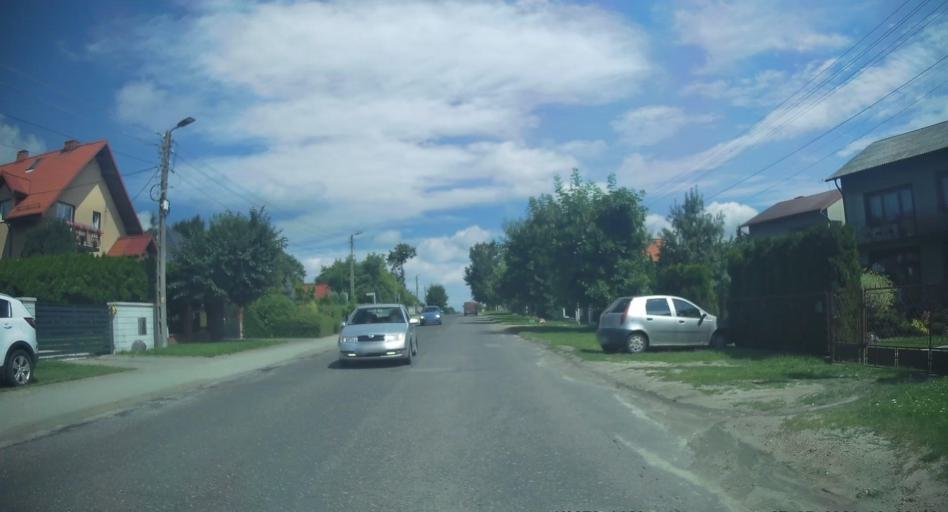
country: PL
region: Lodz Voivodeship
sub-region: Powiat rawski
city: Rawa Mazowiecka
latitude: 51.7489
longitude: 20.2394
